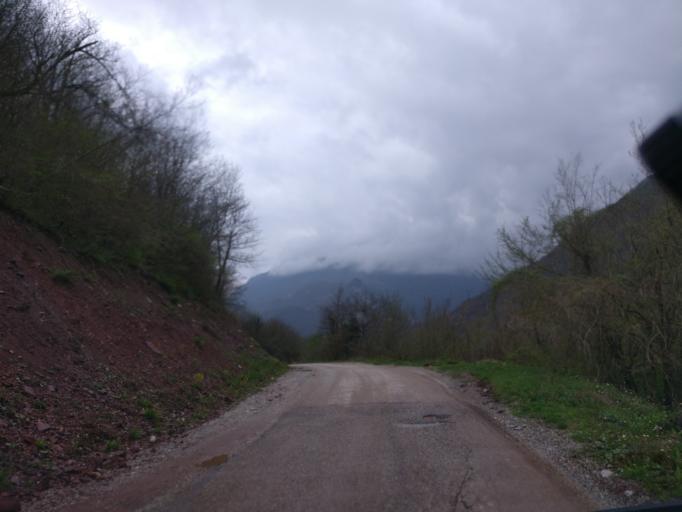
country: BA
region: Republika Srpska
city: Foca
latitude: 43.3550
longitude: 18.8187
